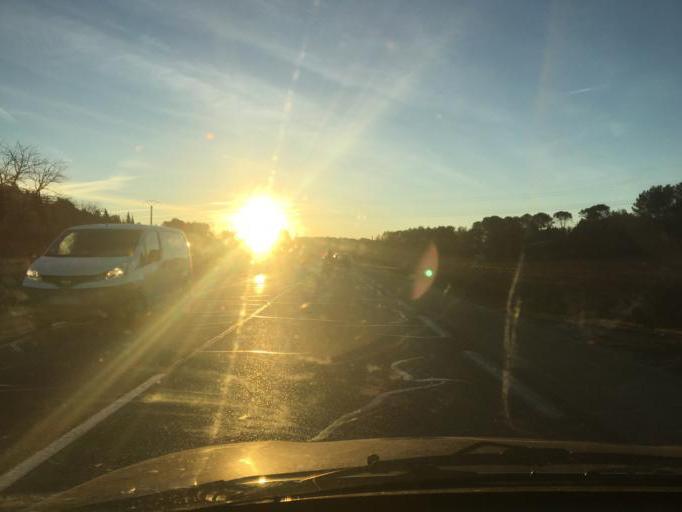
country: FR
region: Provence-Alpes-Cote d'Azur
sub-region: Departement du Var
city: Lorgues
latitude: 43.4693
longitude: 6.3835
